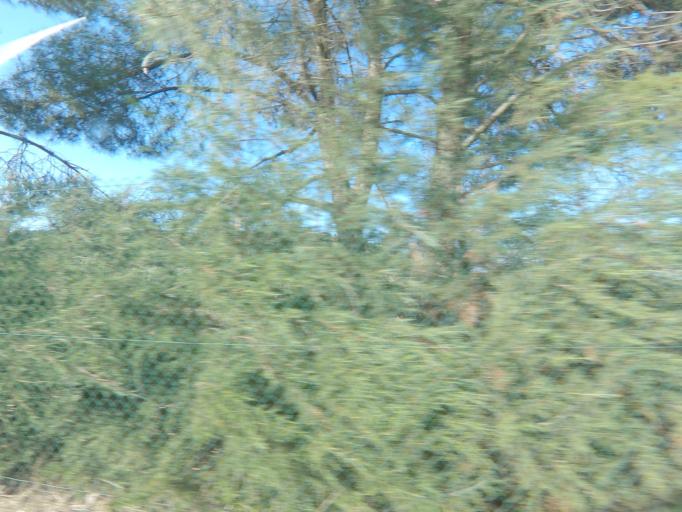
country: PT
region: Vila Real
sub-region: Sabrosa
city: Vilela
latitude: 41.2223
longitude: -7.6000
